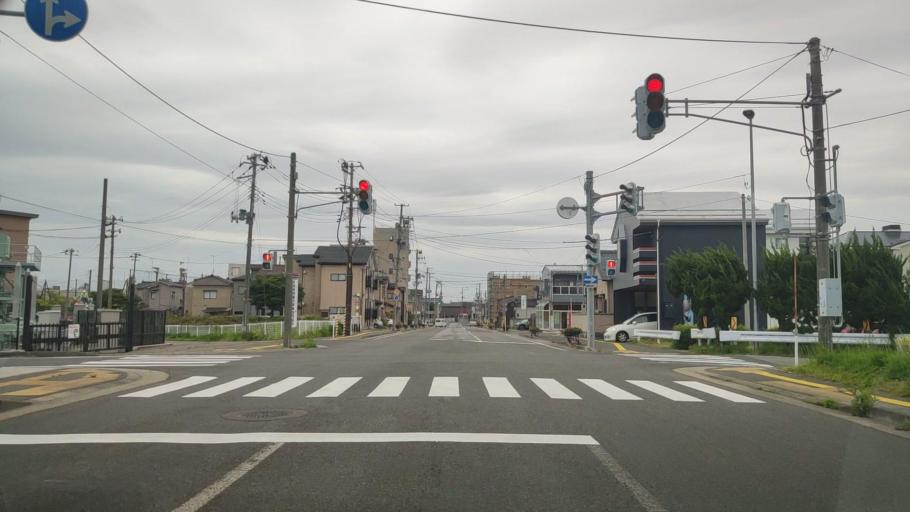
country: JP
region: Niigata
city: Niigata-shi
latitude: 37.9264
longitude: 139.0669
